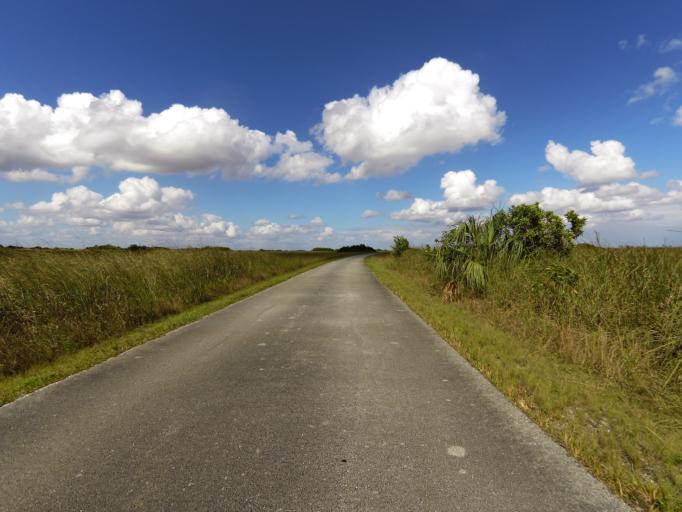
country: US
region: Florida
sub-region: Miami-Dade County
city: The Hammocks
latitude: 25.6799
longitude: -80.7631
